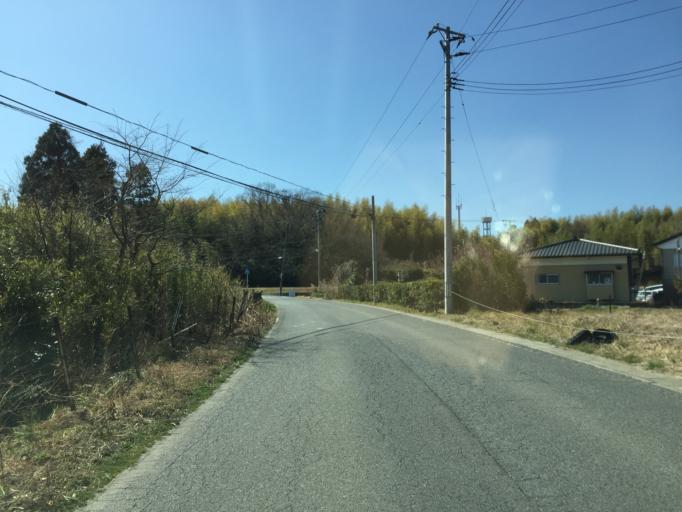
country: JP
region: Fukushima
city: Iwaki
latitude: 37.0573
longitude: 140.8403
